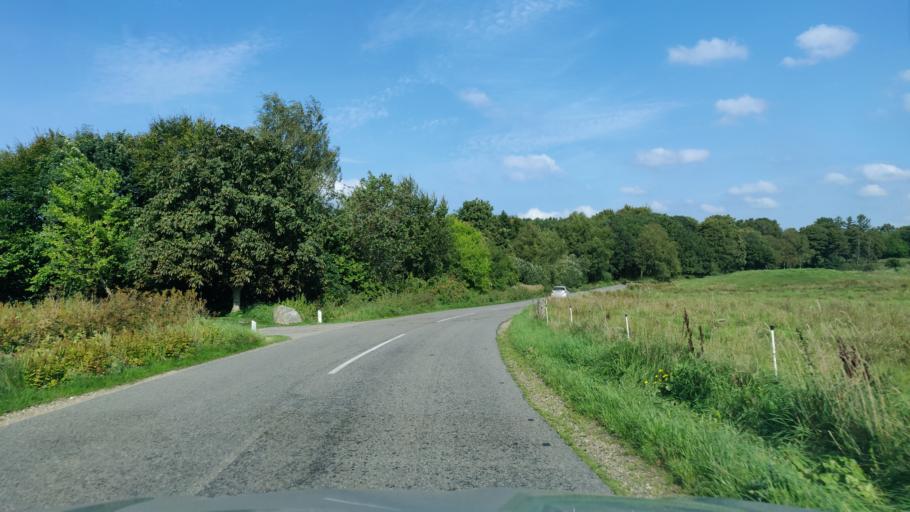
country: DK
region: Central Jutland
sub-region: Herning Kommune
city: Avlum
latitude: 56.2435
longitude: 8.8736
